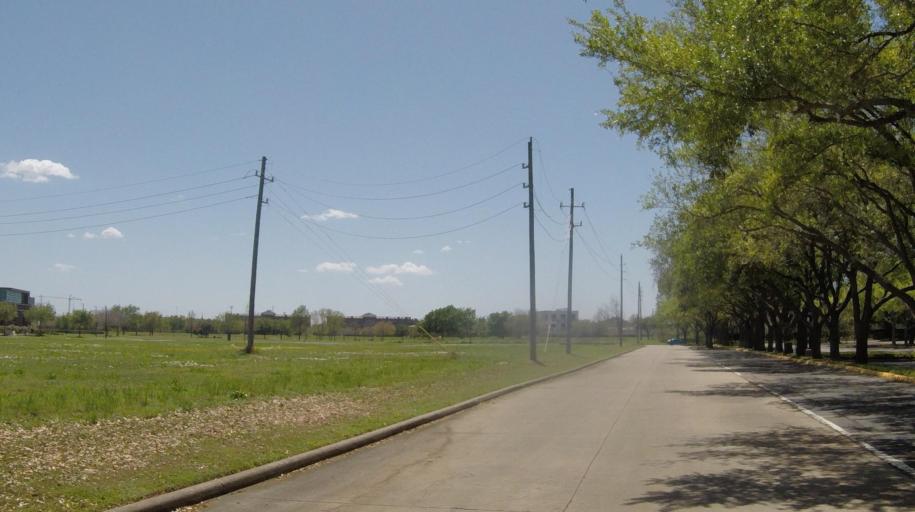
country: US
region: Texas
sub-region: Fort Bend County
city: Sugar Land
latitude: 29.6044
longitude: -95.6264
